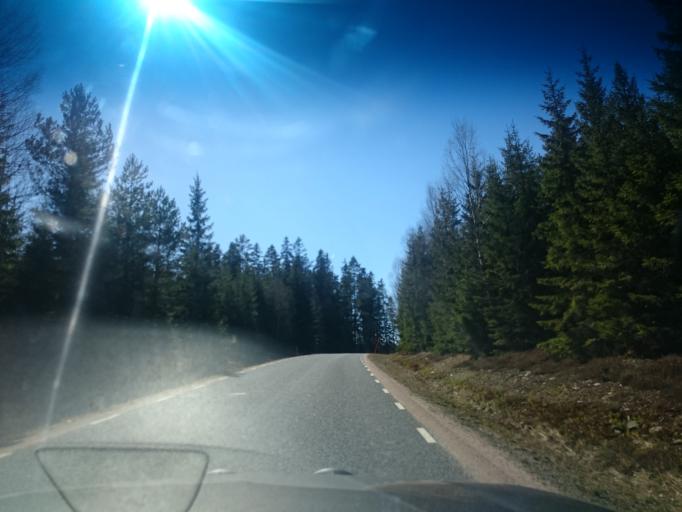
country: SE
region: Joenkoeping
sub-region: Vetlanda Kommun
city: Vetlanda
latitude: 57.2639
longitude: 15.0875
